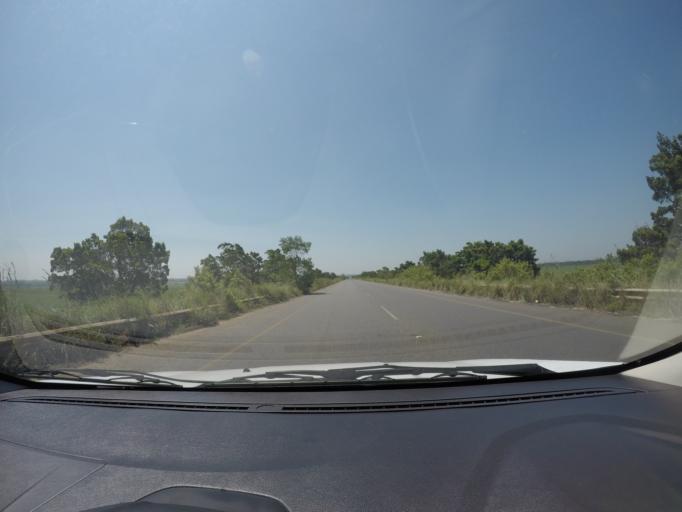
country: ZA
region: KwaZulu-Natal
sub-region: uThungulu District Municipality
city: Empangeni
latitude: -28.7903
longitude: 31.9581
